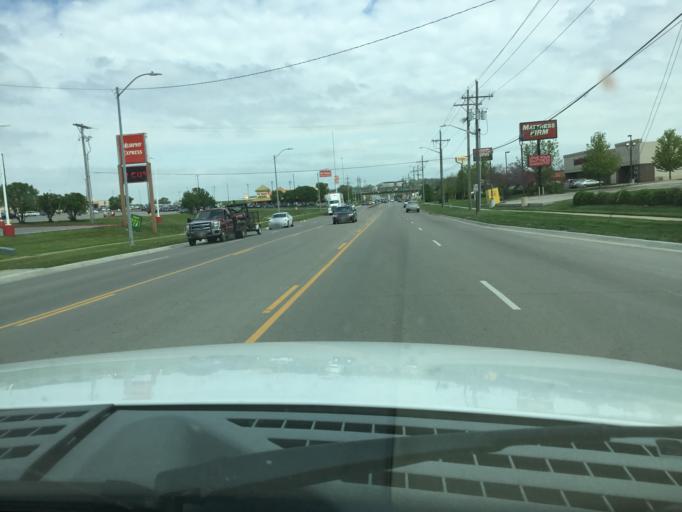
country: US
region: Kansas
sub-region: Shawnee County
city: Topeka
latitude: 39.0382
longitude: -95.7619
